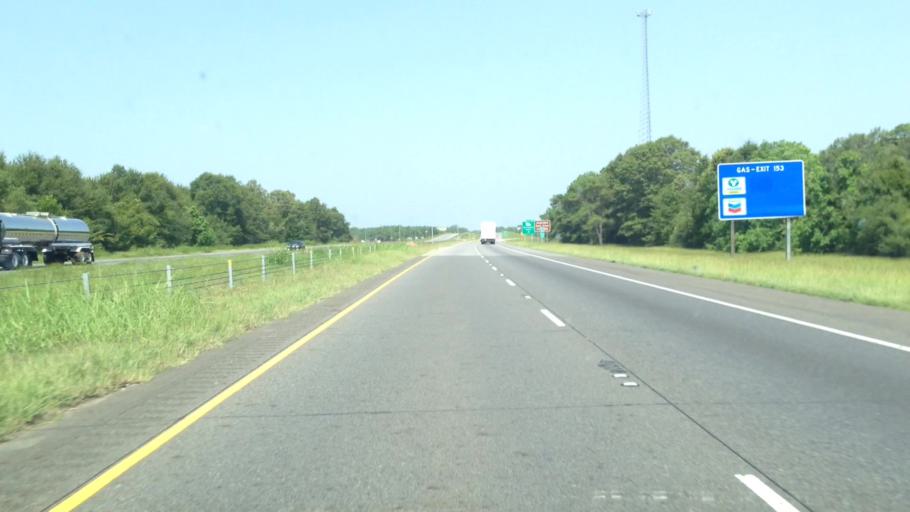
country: US
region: Louisiana
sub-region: Richland Parish
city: Delhi
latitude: 32.4415
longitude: -91.4852
